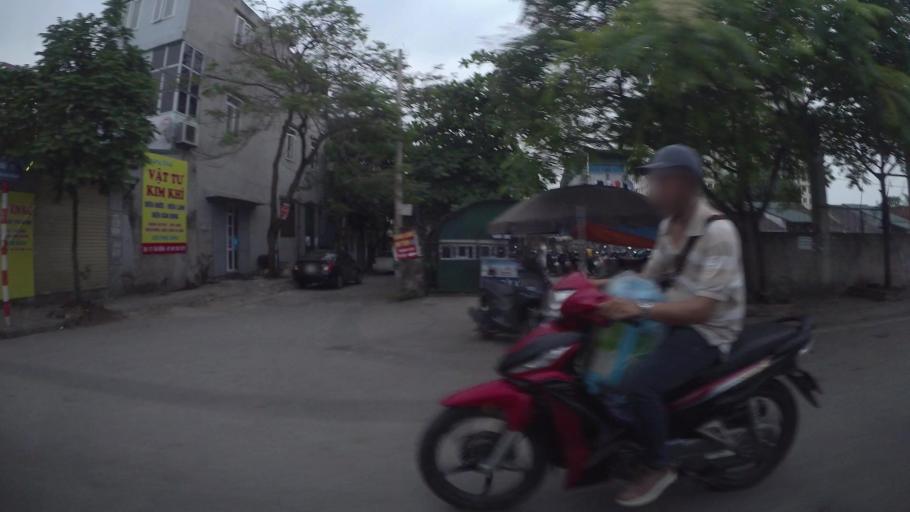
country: VN
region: Ha Noi
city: Trau Quy
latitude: 21.0374
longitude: 105.9118
